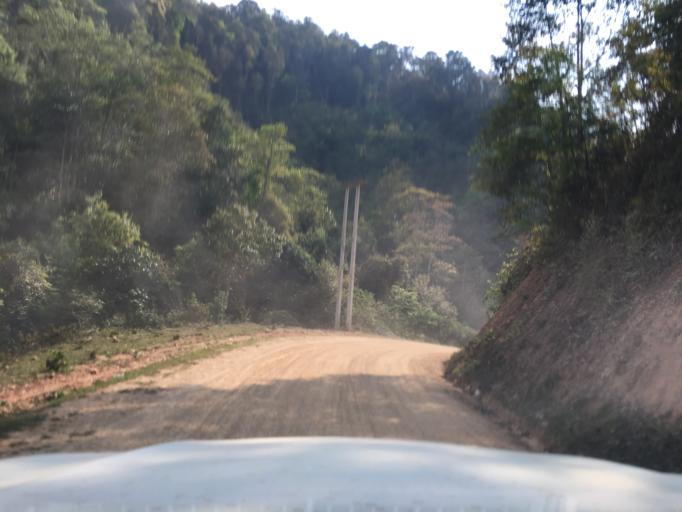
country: LA
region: Houaphan
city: Huameung
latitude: 20.2030
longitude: 103.8458
